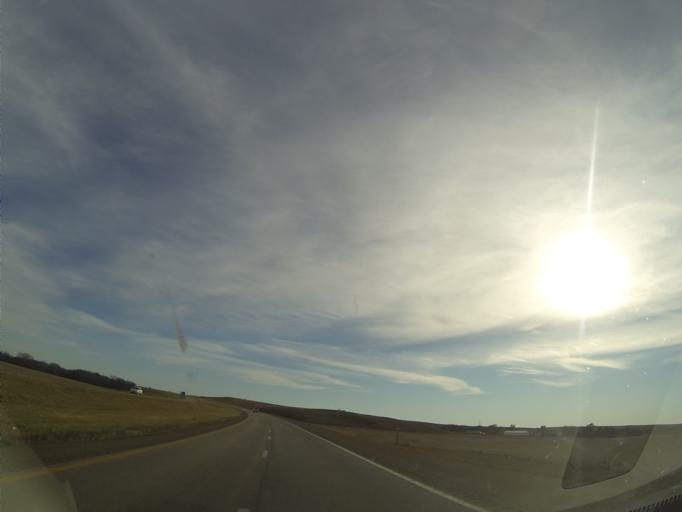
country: US
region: Kansas
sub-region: Ottawa County
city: Minneapolis
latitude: 39.0453
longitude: -97.6516
